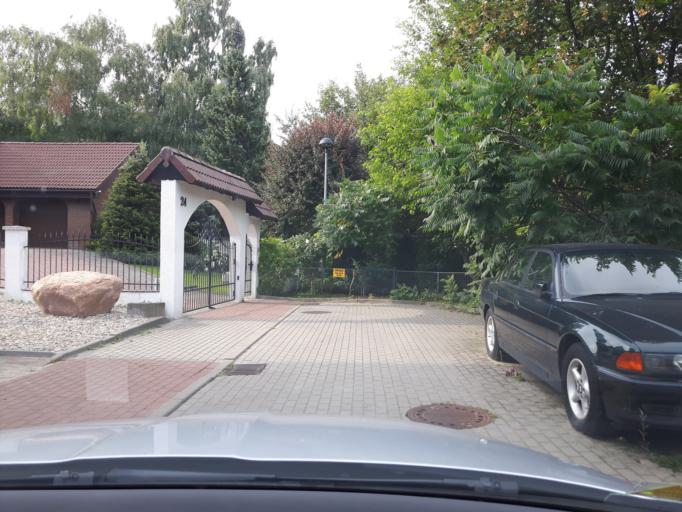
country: PL
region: Pomeranian Voivodeship
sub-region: Gdynia
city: Gdynia
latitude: 54.5042
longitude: 18.5464
